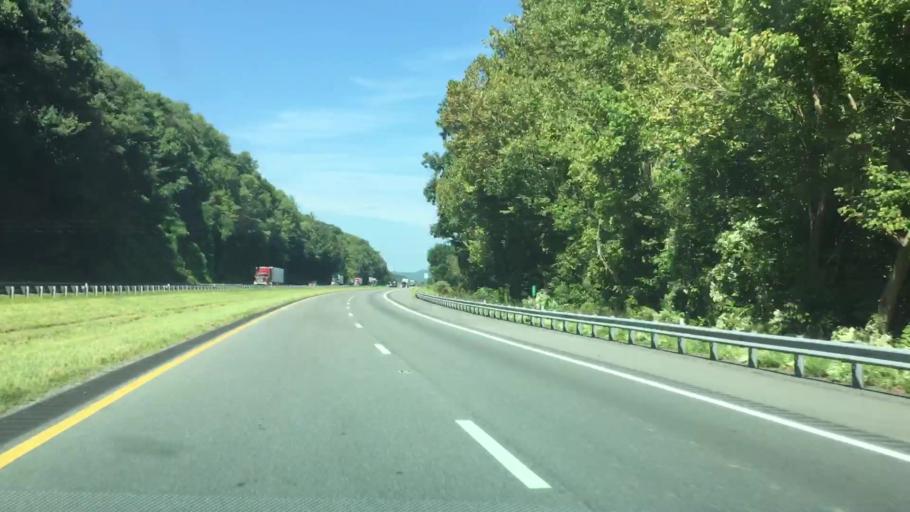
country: US
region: Virginia
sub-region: Smyth County
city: Adwolf
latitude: 36.8089
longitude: -81.6274
